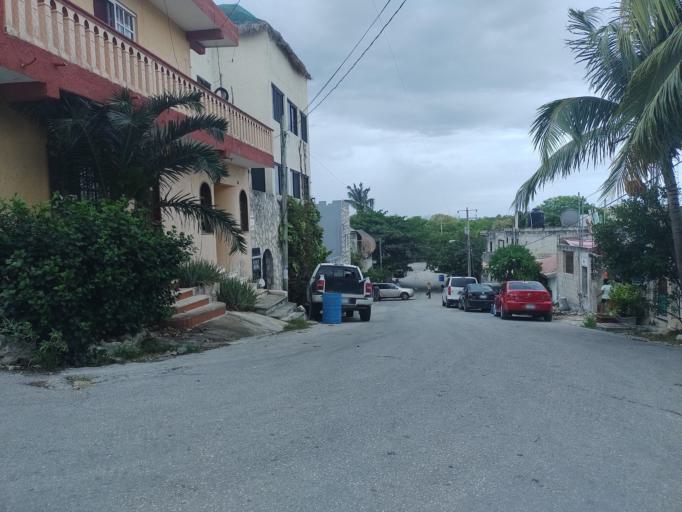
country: MX
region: Quintana Roo
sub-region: Tulum
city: Ciudad Chemuyil
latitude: 20.4000
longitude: -87.3215
